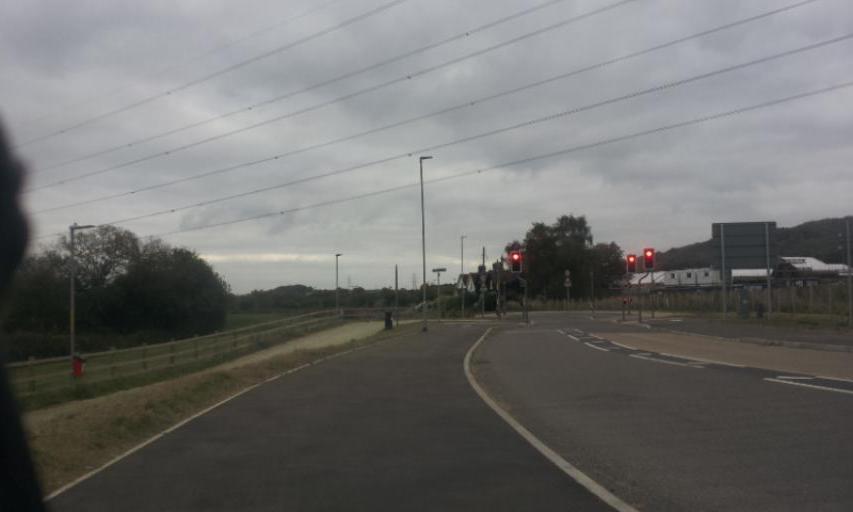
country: GB
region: England
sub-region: Medway
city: Halling
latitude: 51.3423
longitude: 0.4572
